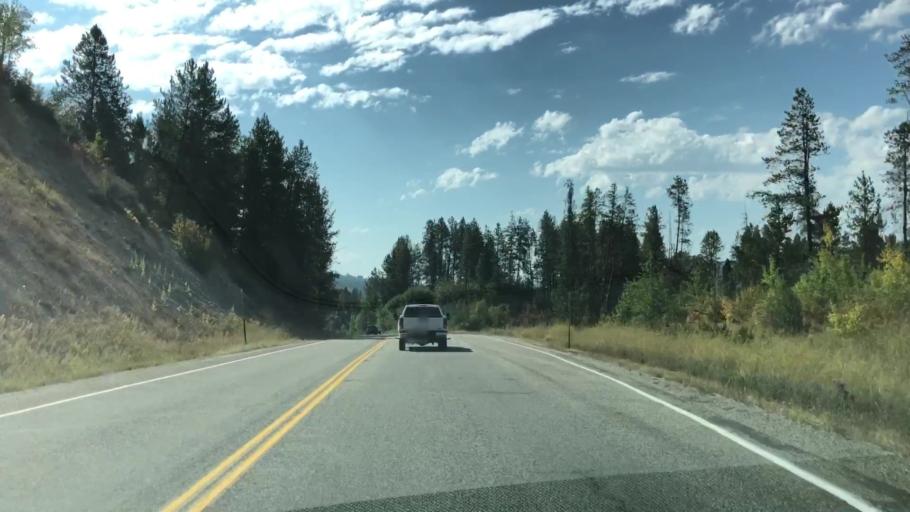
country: US
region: Idaho
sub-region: Teton County
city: Victor
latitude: 43.2872
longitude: -111.1213
